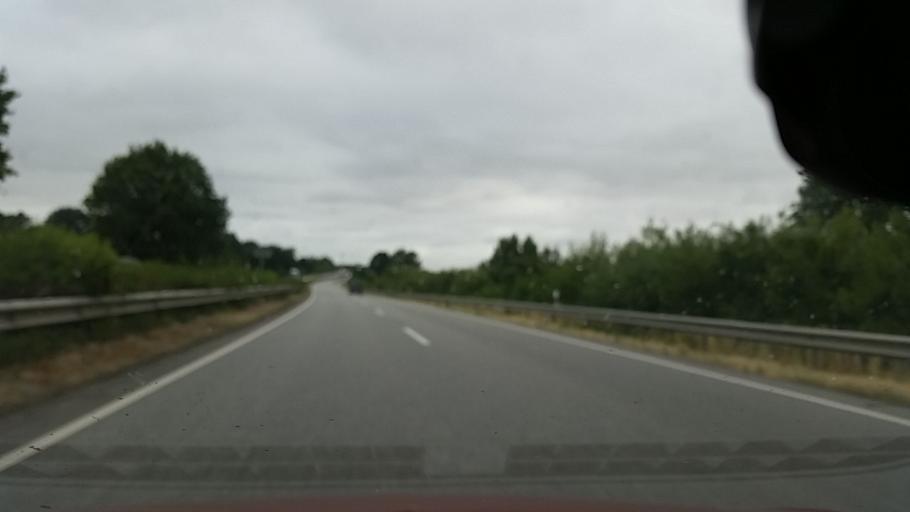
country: DE
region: Schleswig-Holstein
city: Bebensee
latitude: 53.8686
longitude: 10.3104
